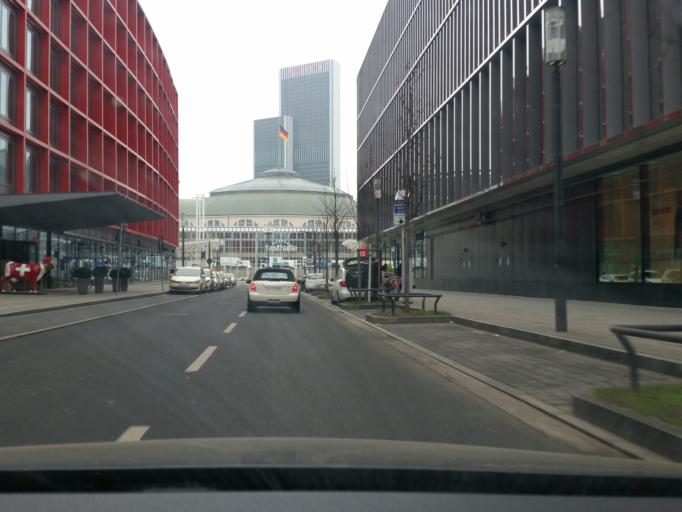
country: DE
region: Hesse
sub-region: Regierungsbezirk Darmstadt
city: Frankfurt am Main
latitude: 50.1093
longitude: 8.6515
